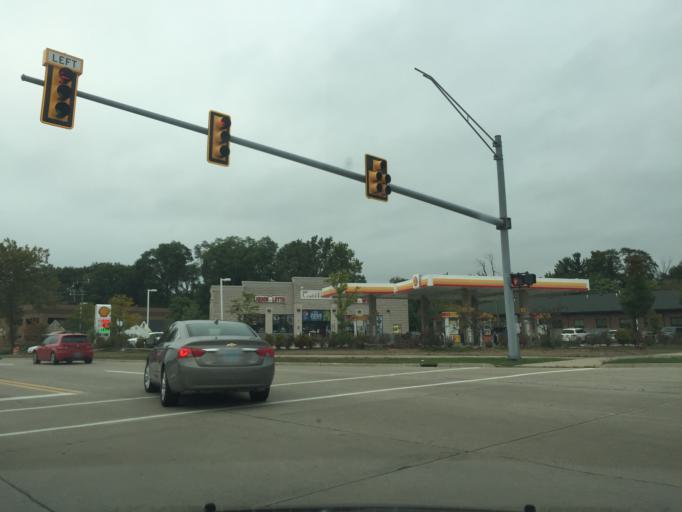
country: US
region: Michigan
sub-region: Oakland County
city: Auburn Hills
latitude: 42.6783
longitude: -83.2461
